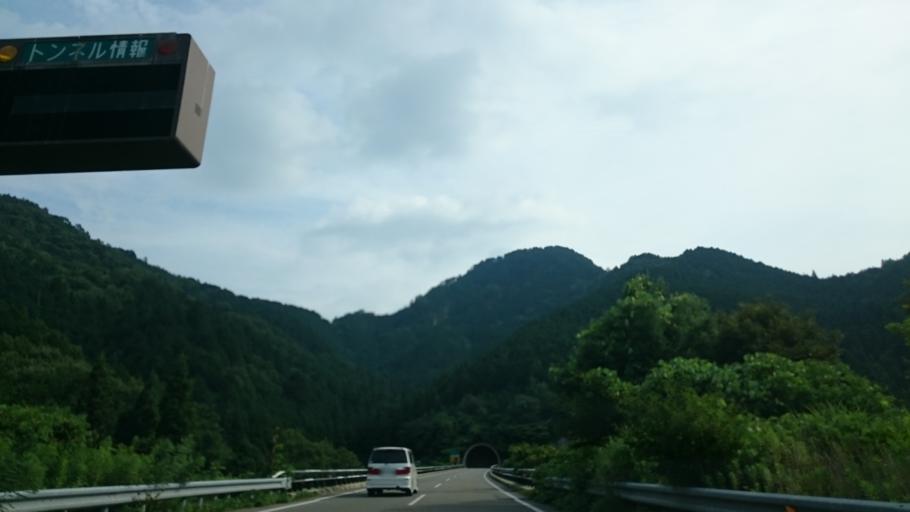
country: JP
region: Gifu
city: Mino
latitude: 35.5677
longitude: 136.9338
